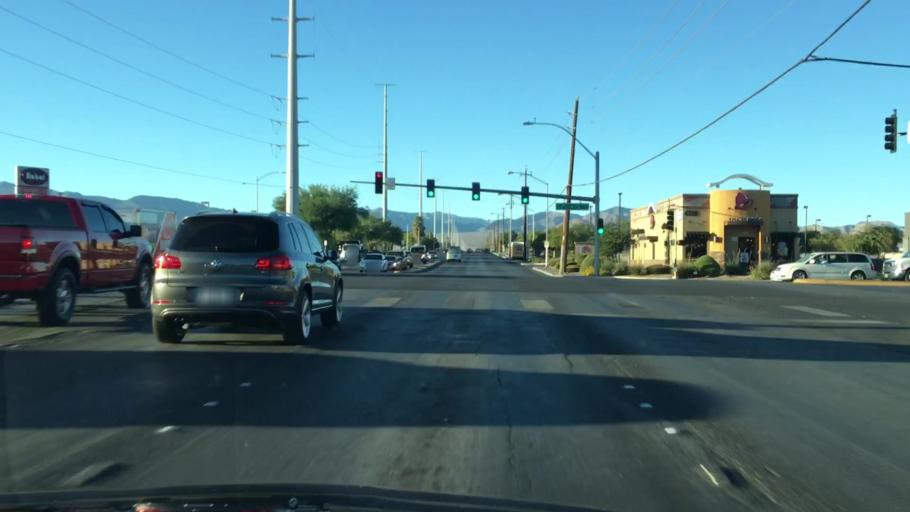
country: US
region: Nevada
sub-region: Clark County
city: Nellis Air Force Base
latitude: 36.2402
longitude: -115.0799
